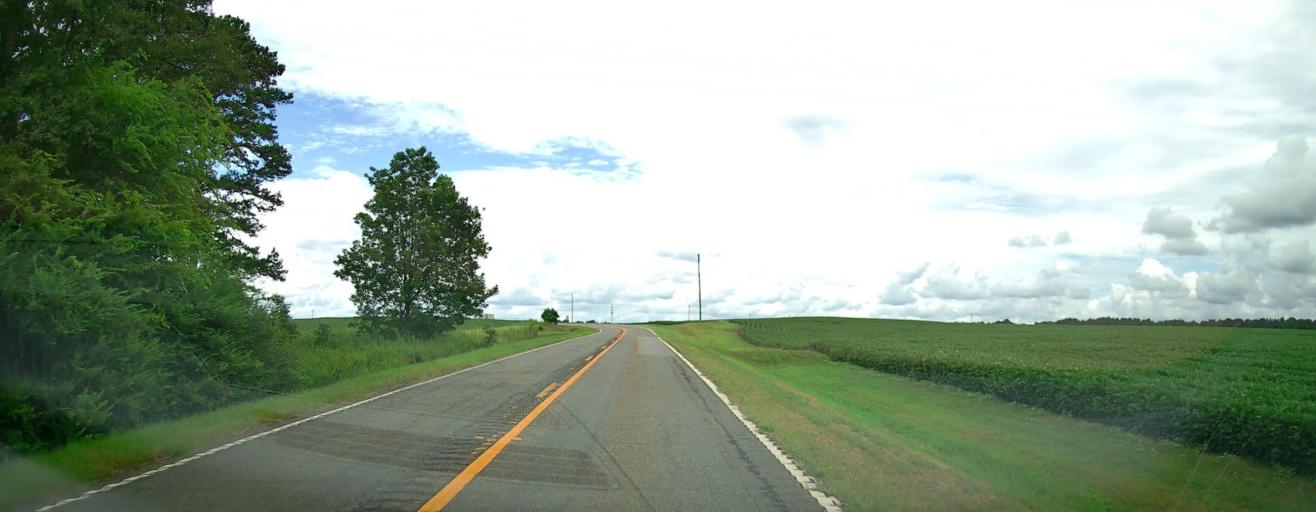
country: US
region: Georgia
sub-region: Dooly County
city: Unadilla
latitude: 32.2877
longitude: -83.8268
